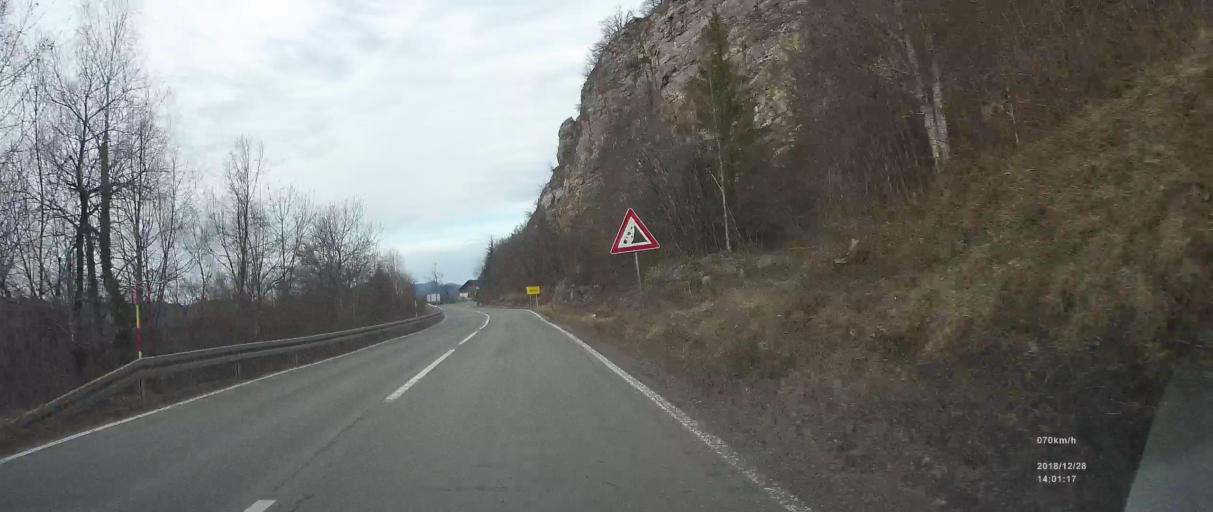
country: SI
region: Kostel
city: Kostel
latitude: 45.4188
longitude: 14.9087
